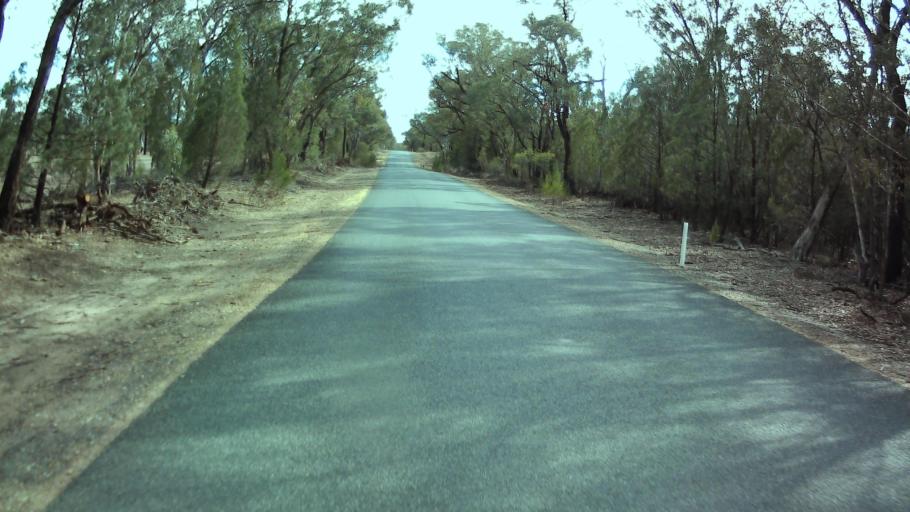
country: AU
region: New South Wales
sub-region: Weddin
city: Grenfell
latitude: -33.8892
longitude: 148.1949
